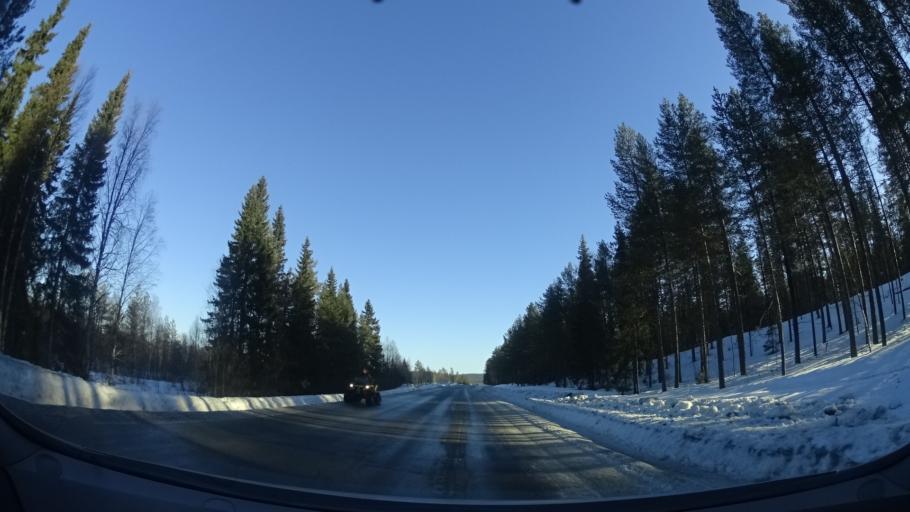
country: SE
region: Vaesterbotten
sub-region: Skelleftea Kommun
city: Langsele
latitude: 65.0458
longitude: 20.0730
